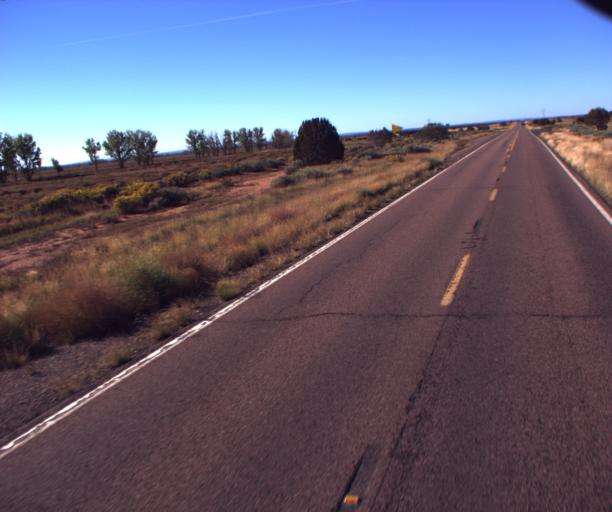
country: US
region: Arizona
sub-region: Navajo County
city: Heber-Overgaard
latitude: 34.6132
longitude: -110.3768
